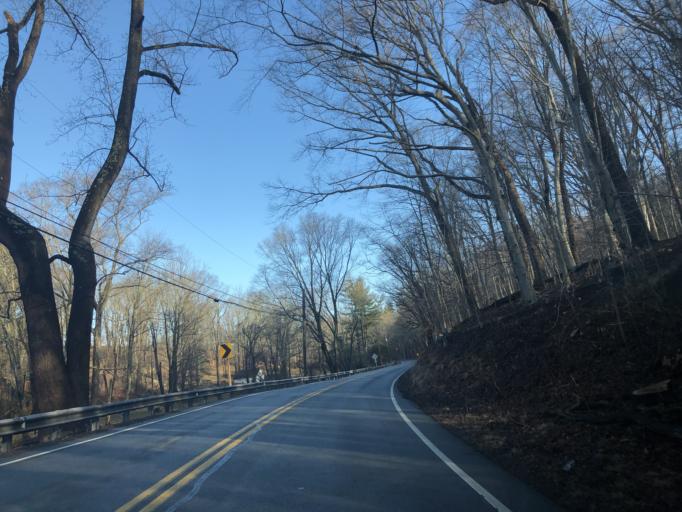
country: US
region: Pennsylvania
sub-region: Delaware County
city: Chester Heights
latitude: 39.8797
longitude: -75.4685
